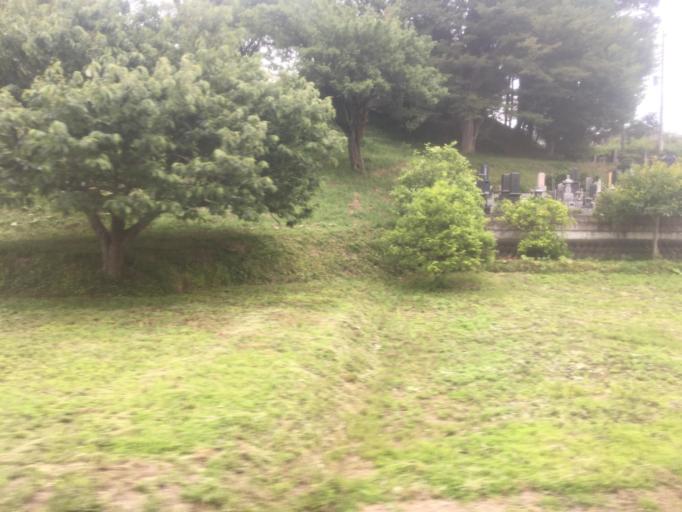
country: JP
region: Gunma
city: Fujioka
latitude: 36.2799
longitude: 139.0376
